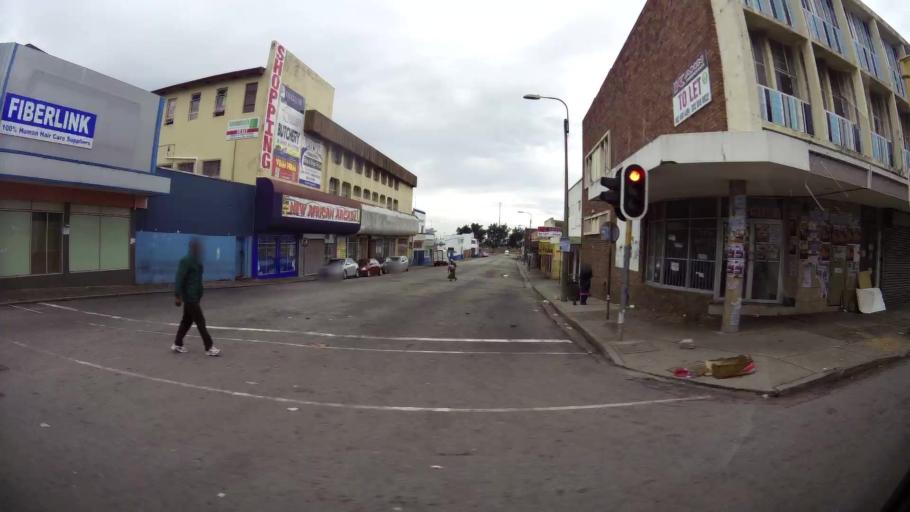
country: ZA
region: Eastern Cape
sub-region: Nelson Mandela Bay Metropolitan Municipality
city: Port Elizabeth
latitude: -33.9495
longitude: 25.6077
